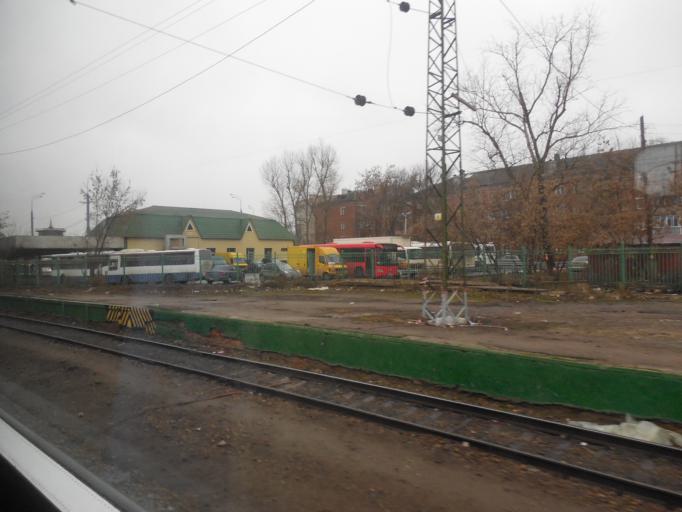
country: RU
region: Moskovskaya
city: Domodedovo
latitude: 55.4408
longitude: 37.7722
